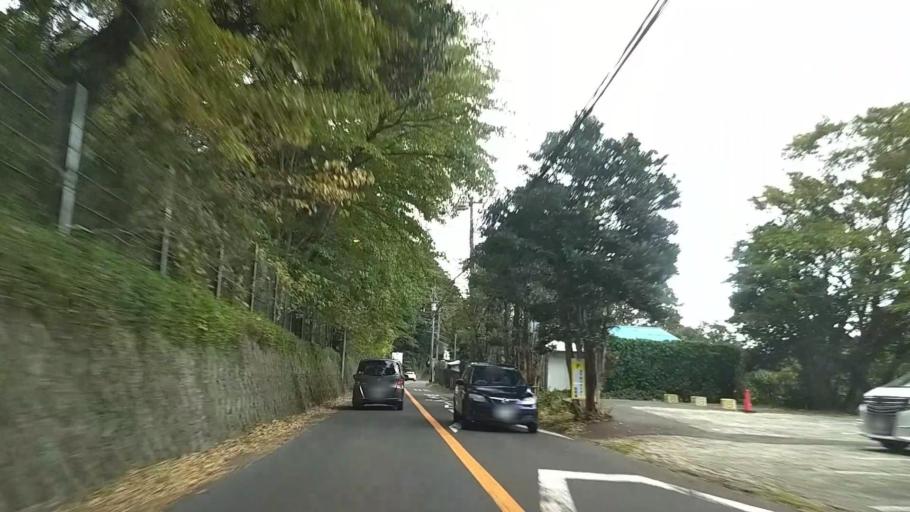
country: JP
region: Kanagawa
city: Odawara
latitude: 35.2017
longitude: 139.1318
